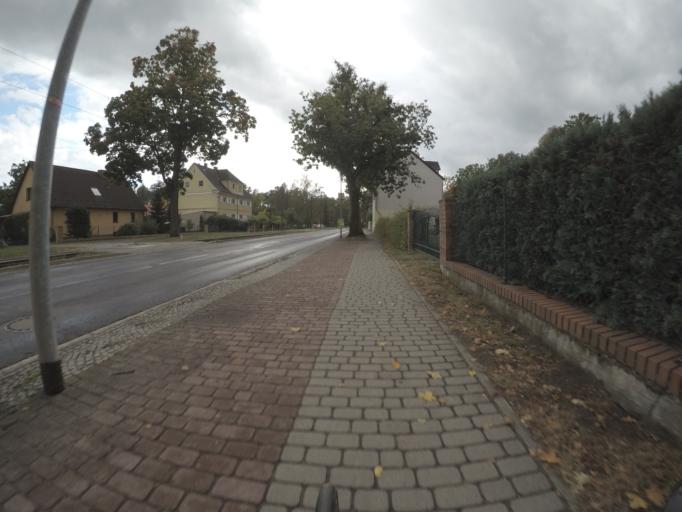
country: DE
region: Brandenburg
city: Schoneiche
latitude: 52.4772
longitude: 13.6939
